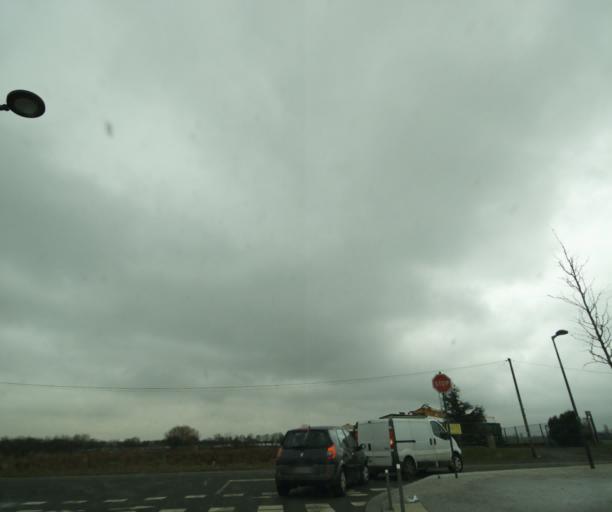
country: FR
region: Ile-de-France
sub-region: Departement de l'Essonne
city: Massy
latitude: 48.7197
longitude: 2.2835
